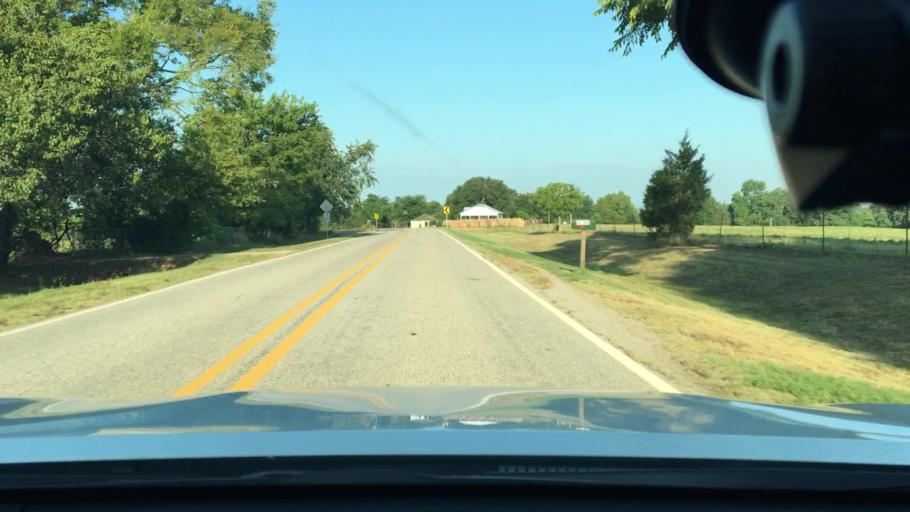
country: US
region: Arkansas
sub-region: Johnson County
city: Coal Hill
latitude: 35.3402
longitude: -93.6019
